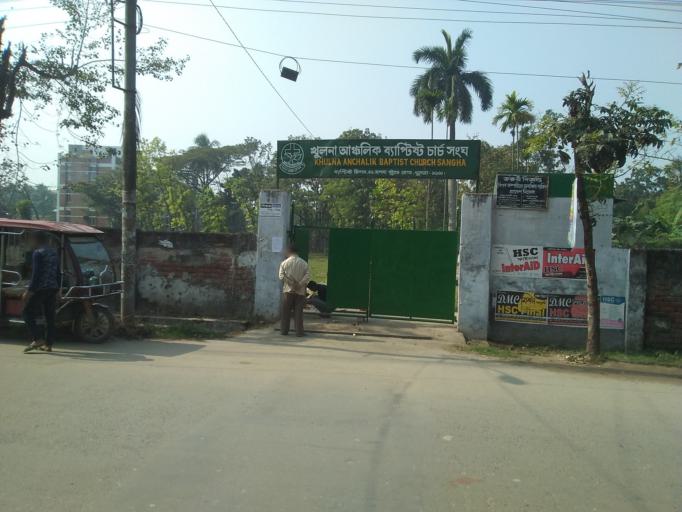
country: BD
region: Khulna
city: Khulna
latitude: 22.8053
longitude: 89.5775
